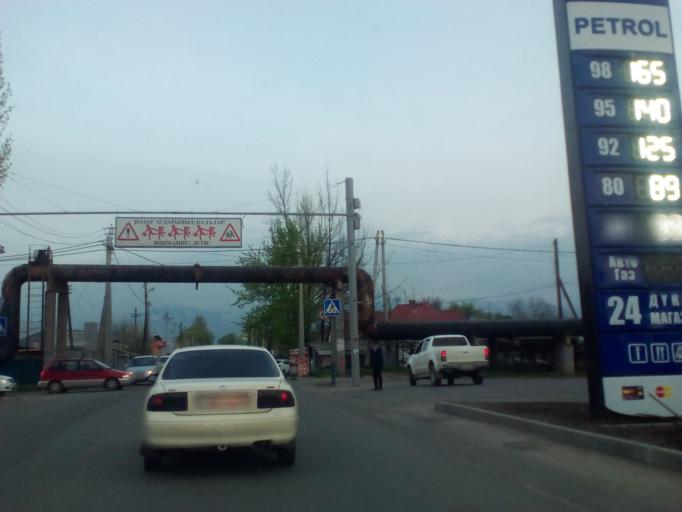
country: KZ
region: Almaty Qalasy
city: Almaty
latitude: 43.2337
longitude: 76.8254
